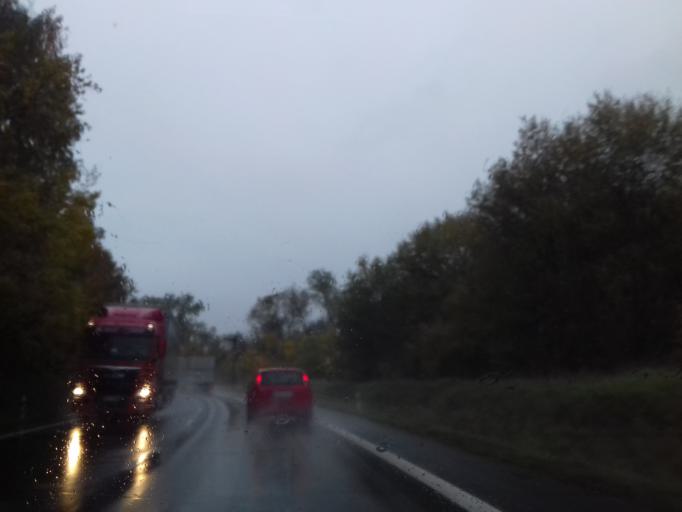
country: CZ
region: Pardubicky
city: Opatov
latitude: 49.7754
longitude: 16.5207
